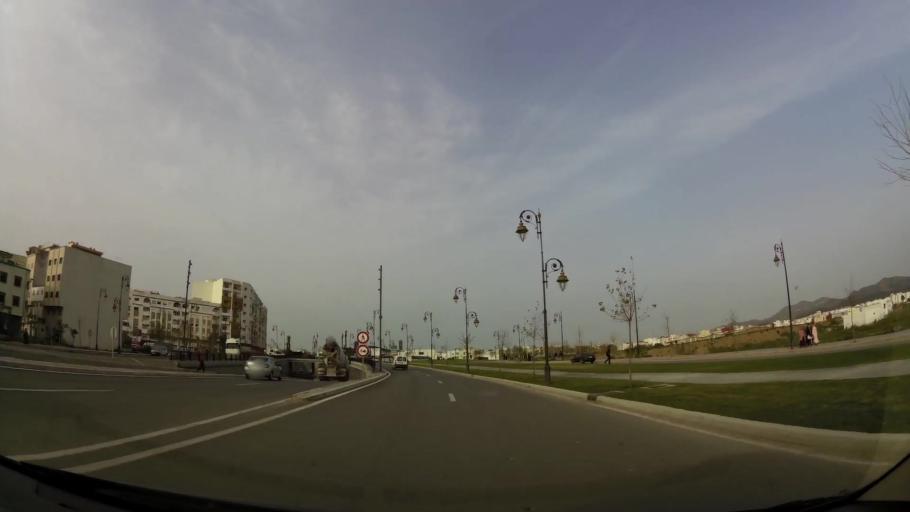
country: MA
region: Tanger-Tetouan
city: Tetouan
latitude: 35.5636
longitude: -5.3549
